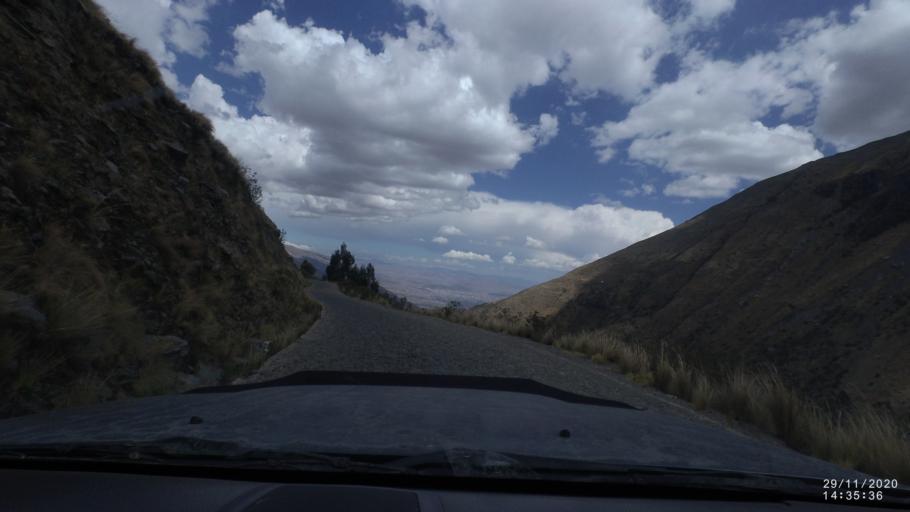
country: BO
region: Cochabamba
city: Sipe Sipe
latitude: -17.2714
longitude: -66.3356
